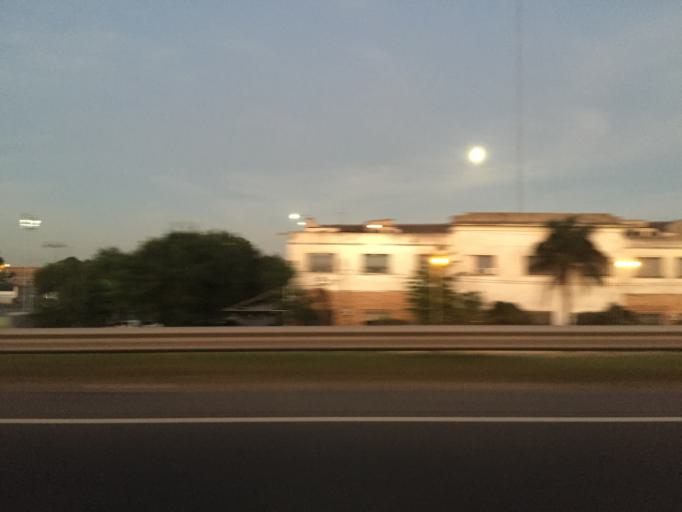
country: AR
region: Buenos Aires F.D.
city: Villa Lugano
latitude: -34.6737
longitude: -58.5027
